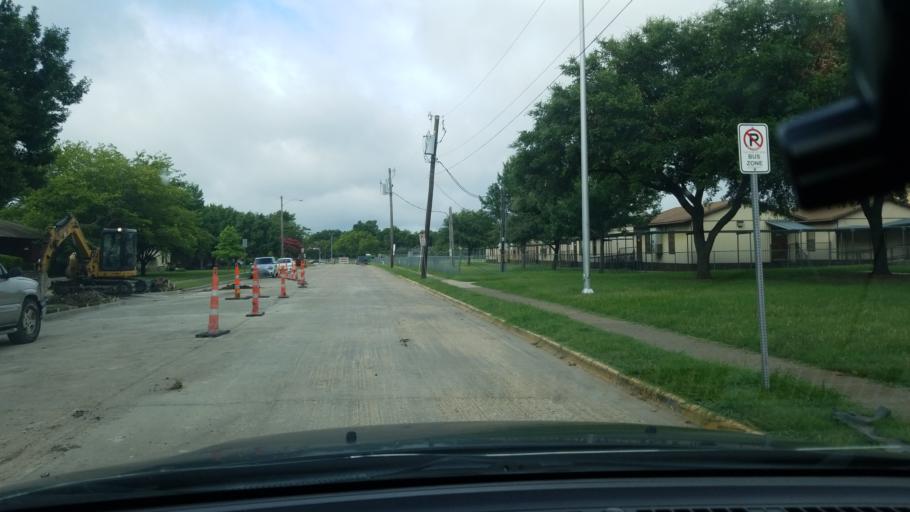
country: US
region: Texas
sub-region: Dallas County
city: Highland Park
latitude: 32.8252
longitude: -96.6930
